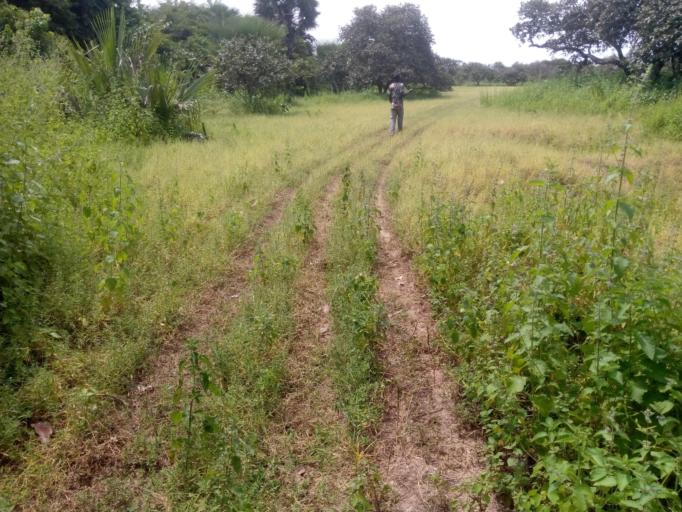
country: GM
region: Western
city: Gunjur
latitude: 13.0600
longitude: -16.7354
